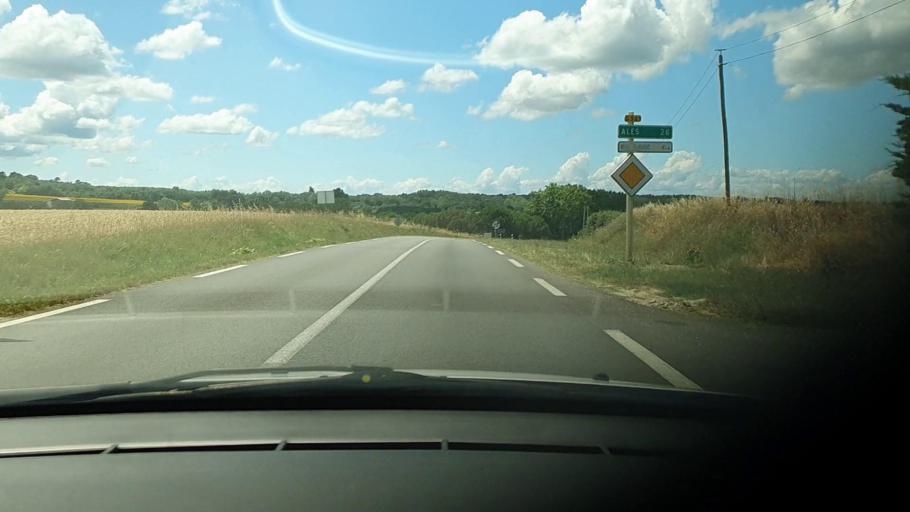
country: FR
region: Languedoc-Roussillon
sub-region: Departement du Gard
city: Montaren-et-Saint-Mediers
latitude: 44.0390
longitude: 4.3486
